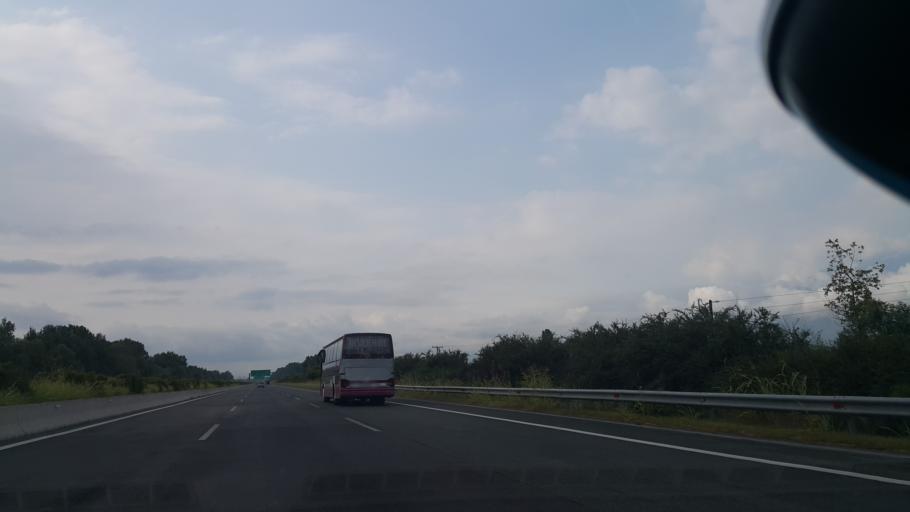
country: GR
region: Central Macedonia
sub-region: Nomos Pierias
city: Nea Efesos
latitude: 40.2118
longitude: 22.5439
